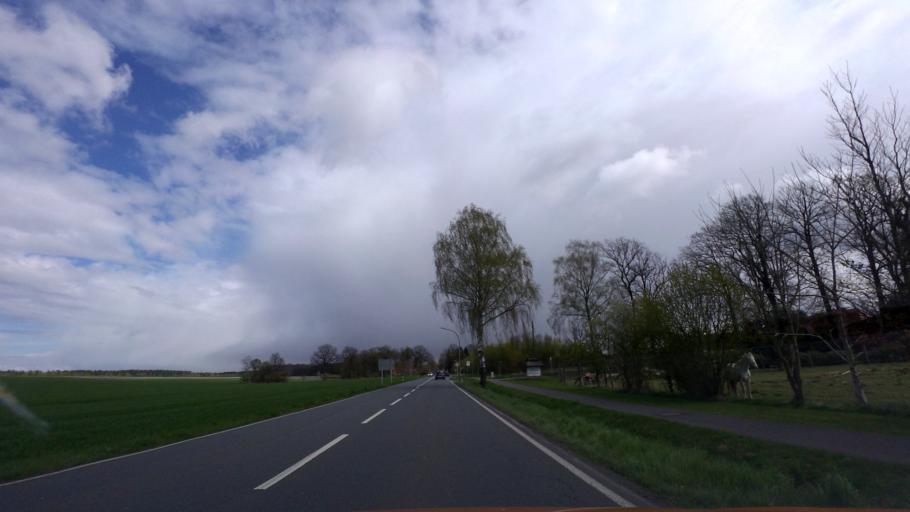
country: DE
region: Lower Saxony
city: Schneverdingen
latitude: 53.0818
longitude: 9.8647
